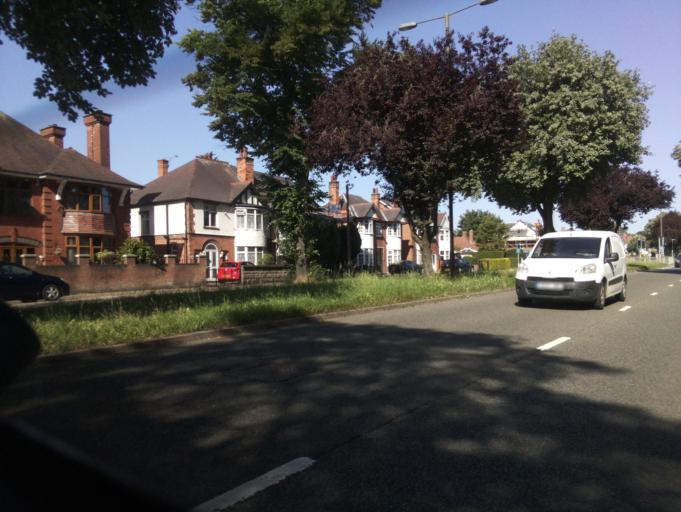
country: GB
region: England
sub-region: Derby
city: Derby
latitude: 52.9032
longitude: -1.4943
